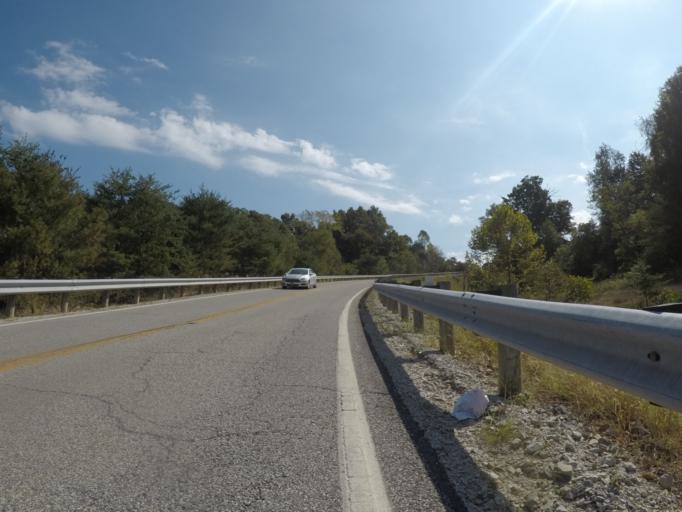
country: US
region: West Virginia
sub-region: Cabell County
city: Lesage
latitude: 38.5911
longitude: -82.4278
